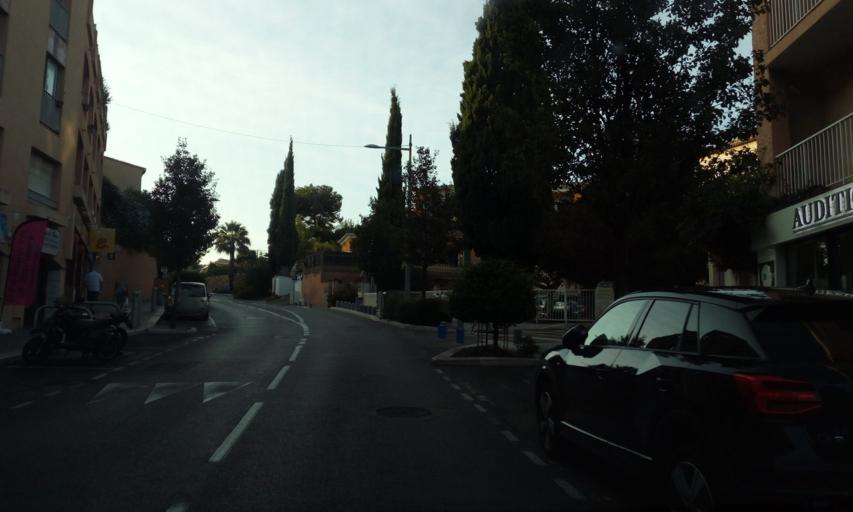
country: FR
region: Provence-Alpes-Cote d'Azur
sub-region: Departement du Var
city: Bandol
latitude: 43.1384
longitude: 5.7514
